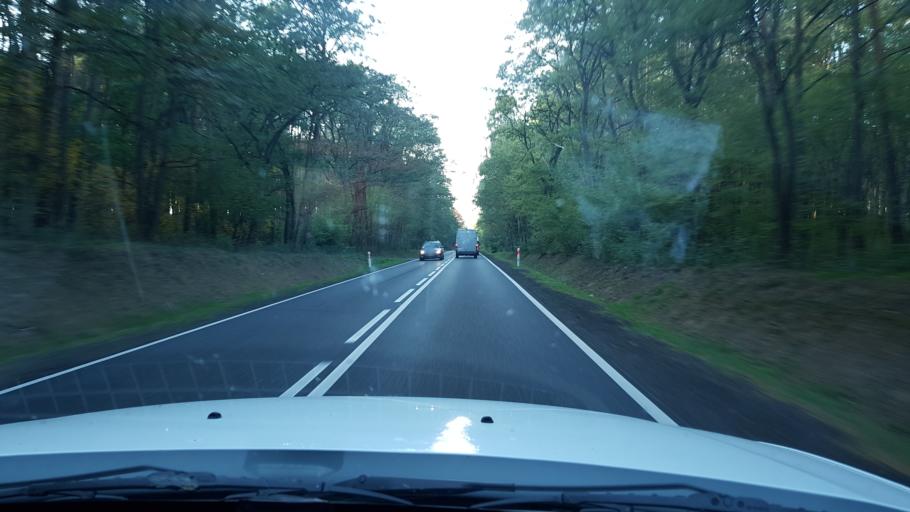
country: PL
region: West Pomeranian Voivodeship
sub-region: Powiat gryfinski
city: Chojna
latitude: 52.9763
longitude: 14.3761
